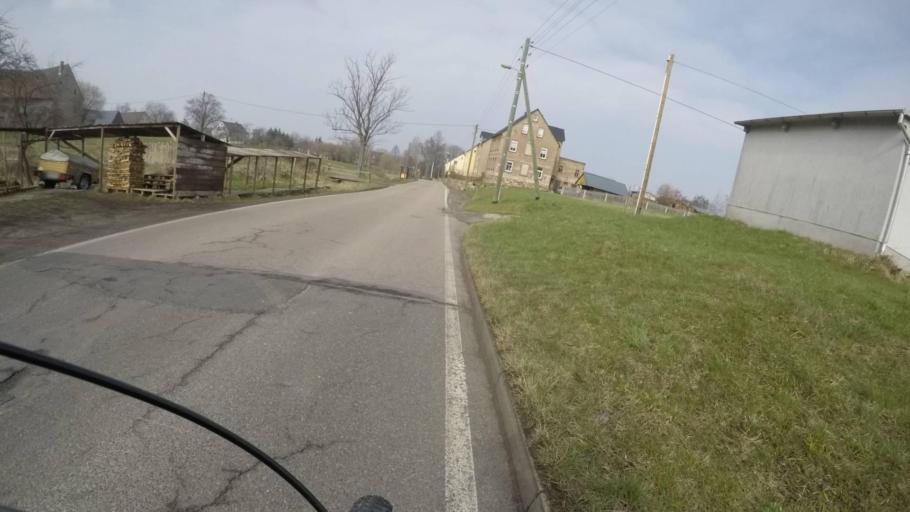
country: DE
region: Saxony
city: Niederfrohna
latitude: 50.8872
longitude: 12.6915
